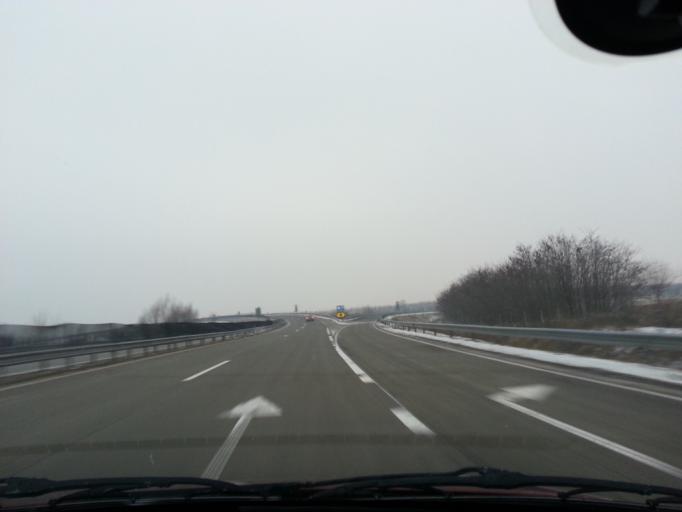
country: HU
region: Pest
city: Nagytarcsa
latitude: 47.5117
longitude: 19.2974
